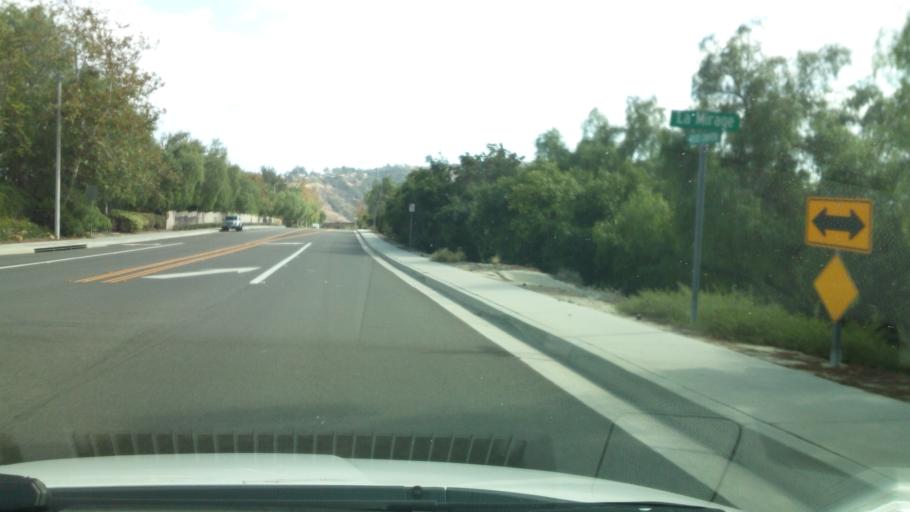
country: US
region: California
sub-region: Orange County
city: Aliso Viejo
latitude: 33.5534
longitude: -117.7308
